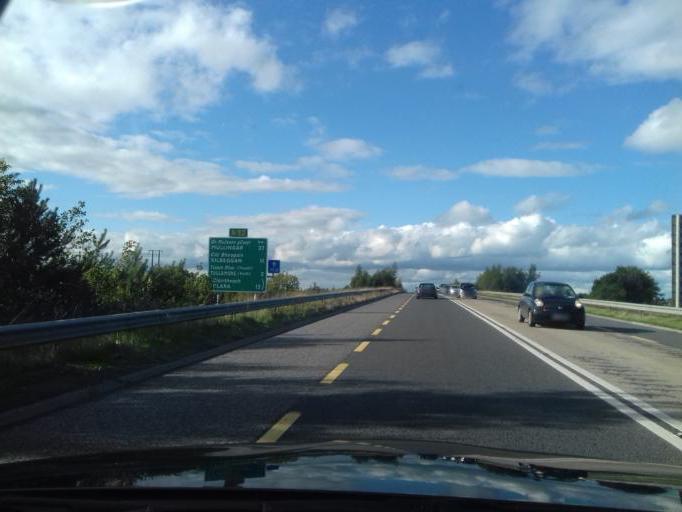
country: IE
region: Leinster
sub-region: Uibh Fhaili
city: Tullamore
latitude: 53.2779
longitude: -7.4679
